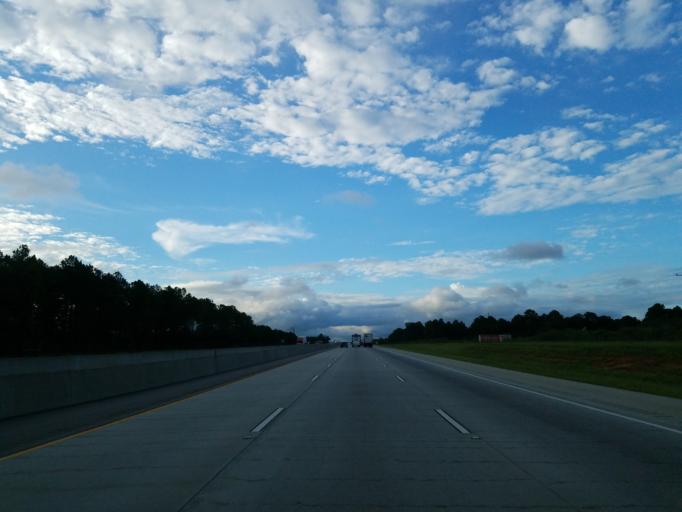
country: US
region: Georgia
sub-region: Tift County
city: Omega
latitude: 31.3219
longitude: -83.4806
